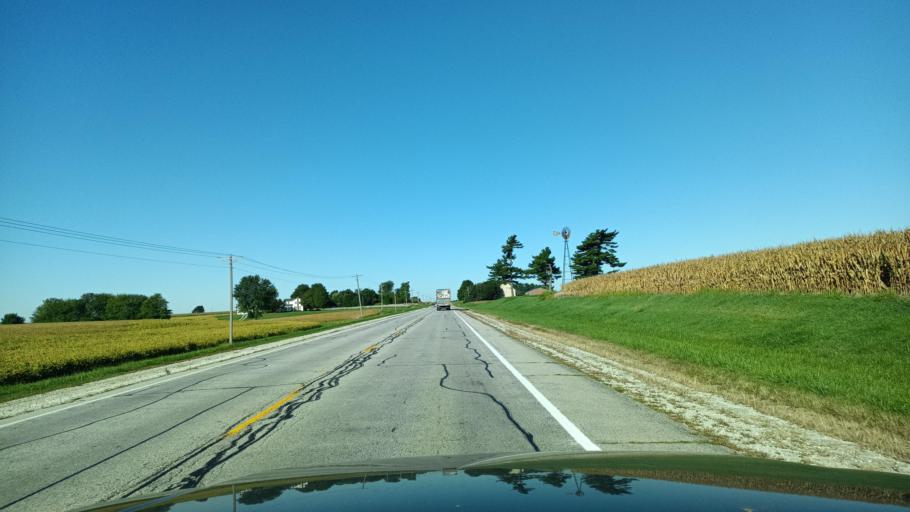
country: US
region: Illinois
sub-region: Warren County
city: Monmouth
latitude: 40.8785
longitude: -90.7068
